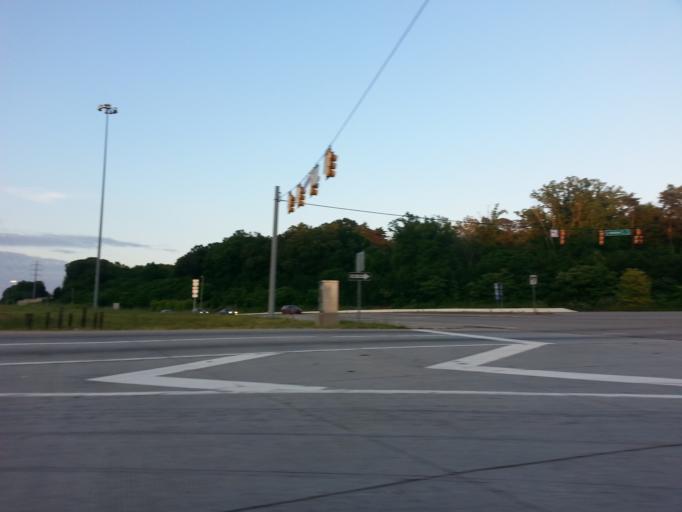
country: US
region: Tennessee
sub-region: Knox County
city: Knoxville
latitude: 35.9399
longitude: -84.0038
